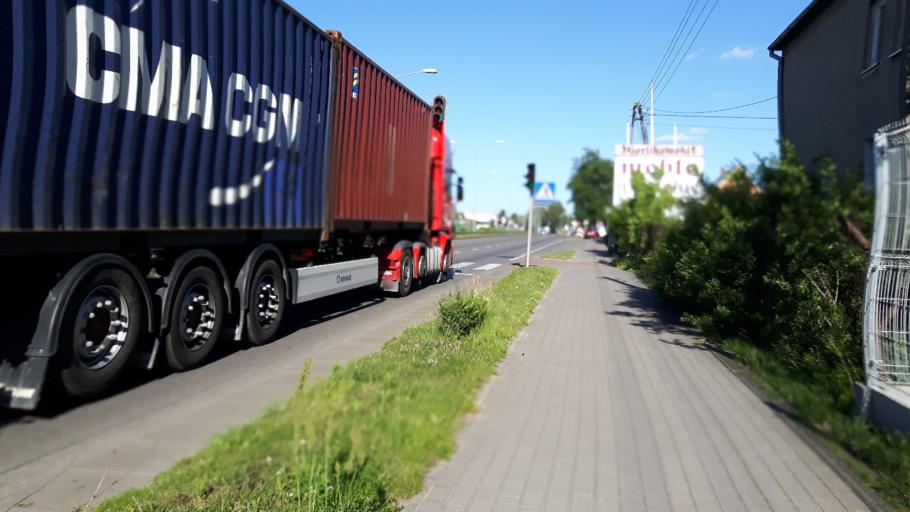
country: PL
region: Pomeranian Voivodeship
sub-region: Powiat wejherowski
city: Wejherowo
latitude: 54.6030
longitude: 18.2668
